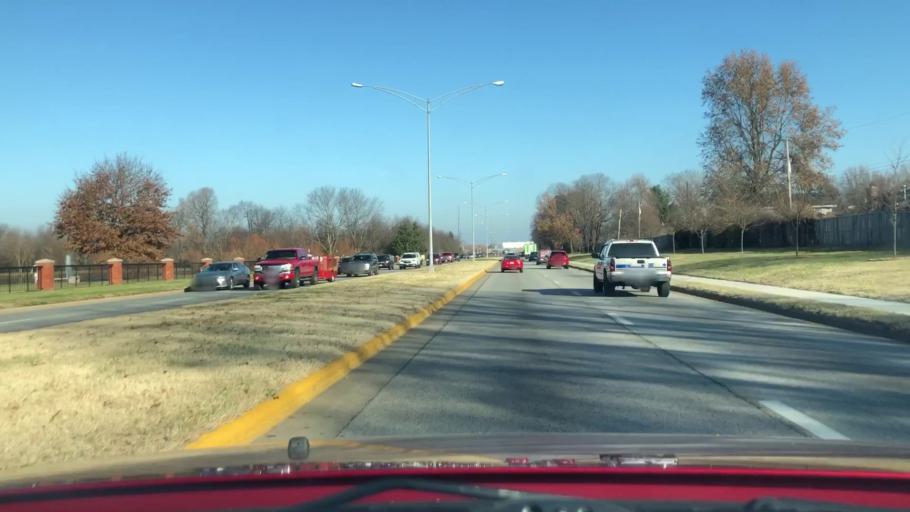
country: US
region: Missouri
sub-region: Greene County
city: Battlefield
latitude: 37.1473
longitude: -93.3192
